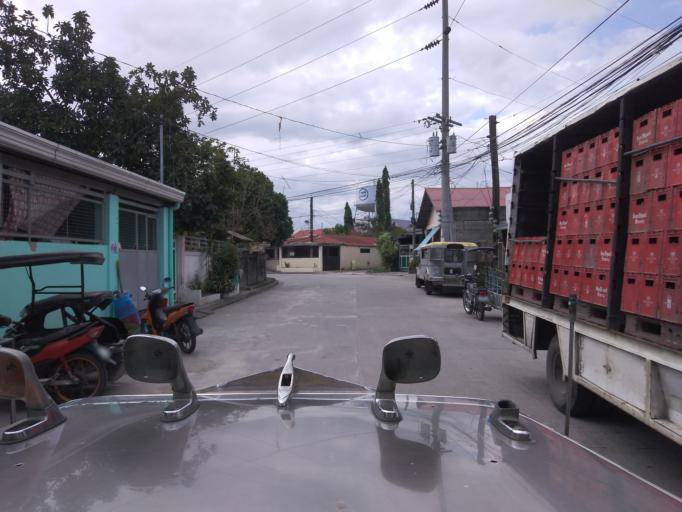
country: PH
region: Central Luzon
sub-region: Province of Pampanga
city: Pandacaqui
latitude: 15.1796
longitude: 120.6491
